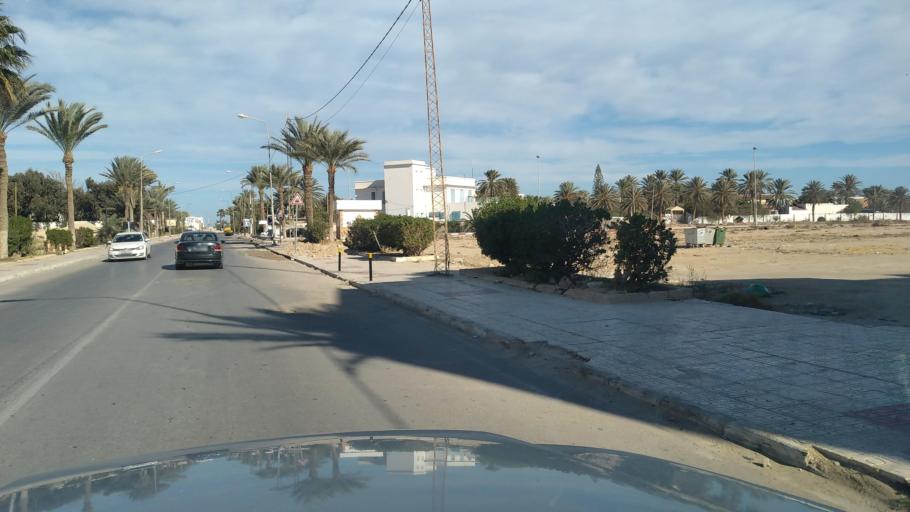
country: TN
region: Qabis
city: Gabes
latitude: 33.8903
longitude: 10.1129
